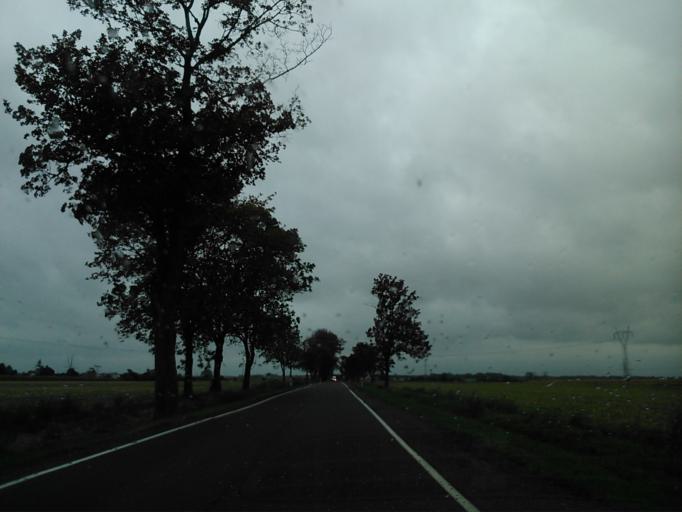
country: PL
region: Kujawsko-Pomorskie
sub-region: Powiat mogilenski
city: Strzelno
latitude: 52.6663
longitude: 18.2427
